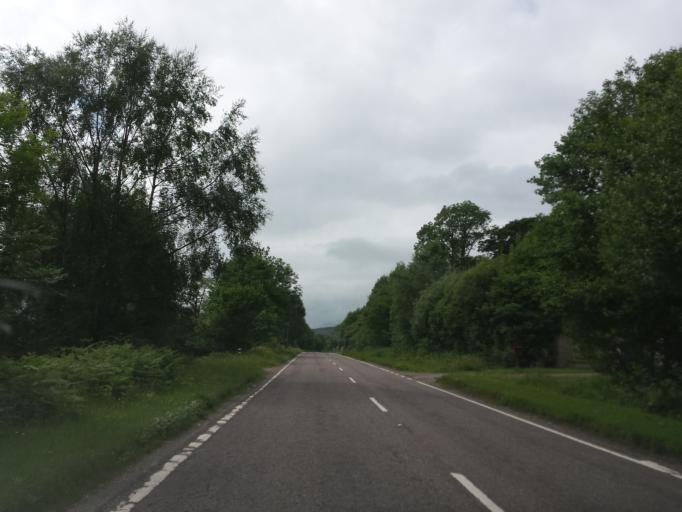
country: GB
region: Scotland
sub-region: Highland
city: Fort William
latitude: 56.8570
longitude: -5.3062
